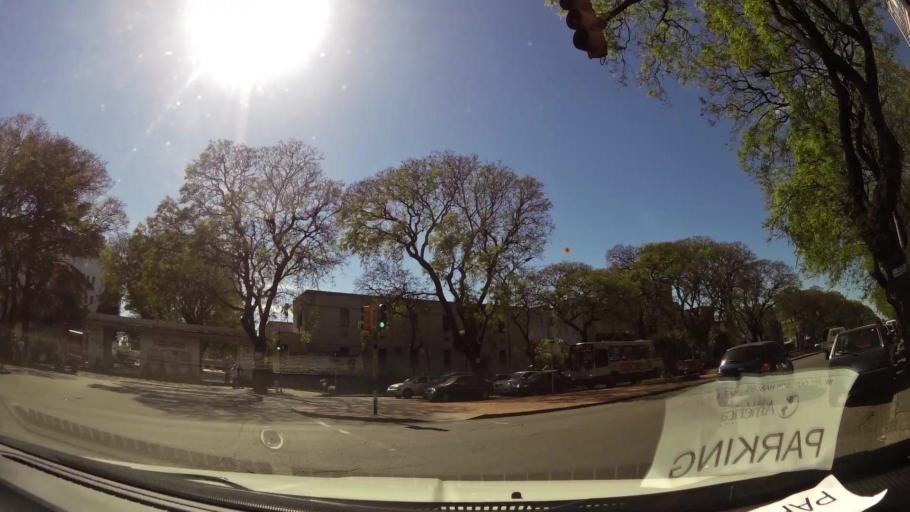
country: UY
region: Montevideo
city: Montevideo
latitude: -34.8990
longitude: -56.1646
